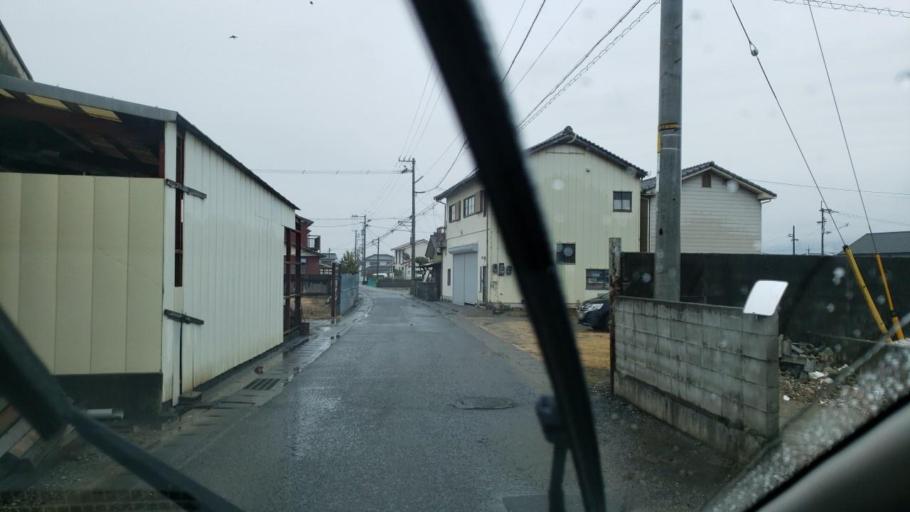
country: JP
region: Tokushima
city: Kamojimacho-jogejima
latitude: 34.0776
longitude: 134.3409
